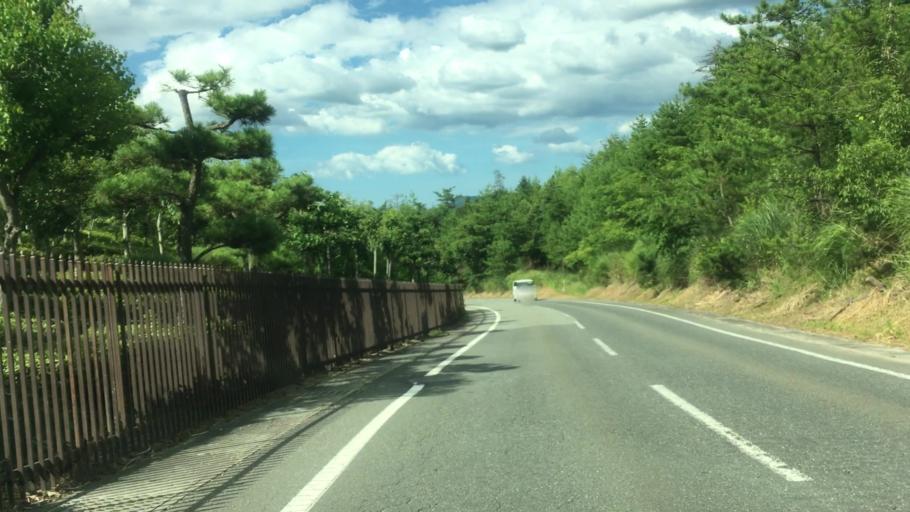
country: JP
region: Hyogo
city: Toyooka
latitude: 35.5185
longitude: 134.7904
